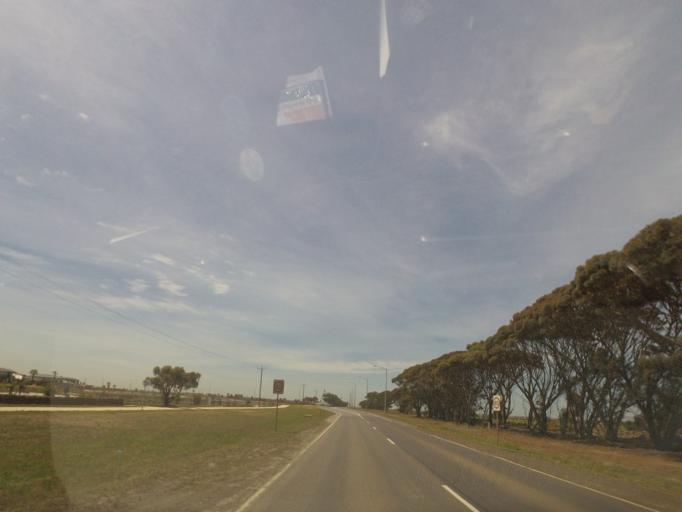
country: AU
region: Victoria
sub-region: Wyndham
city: Wyndham Vale
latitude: -37.8543
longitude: 144.5877
